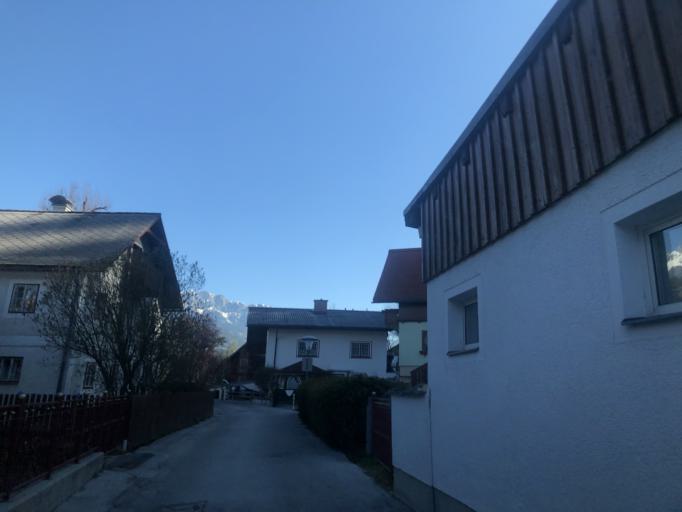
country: AT
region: Styria
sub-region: Politischer Bezirk Liezen
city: Schladming
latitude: 47.3903
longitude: 13.6901
